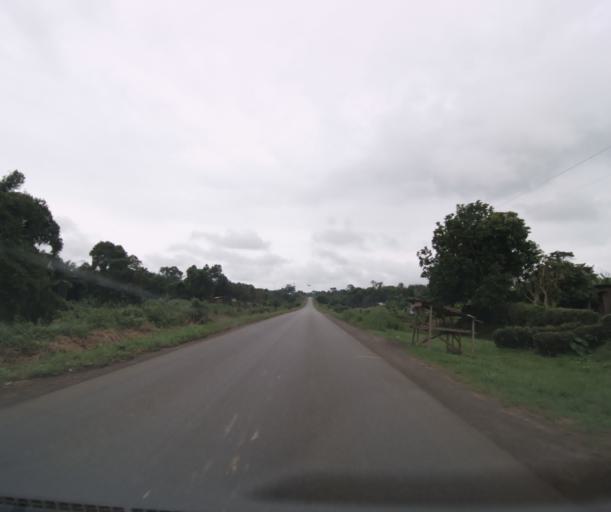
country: CM
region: Littoral
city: Edea
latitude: 3.7337
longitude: 10.1146
